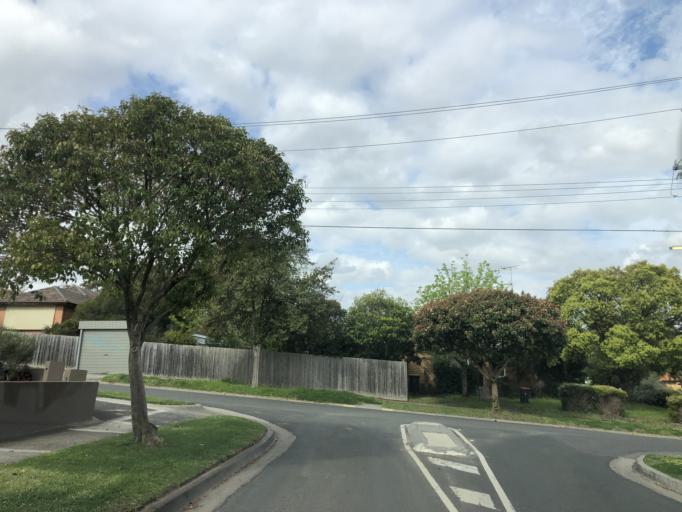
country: AU
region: Victoria
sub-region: Monash
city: Ashwood
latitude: -37.8663
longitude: 145.1089
